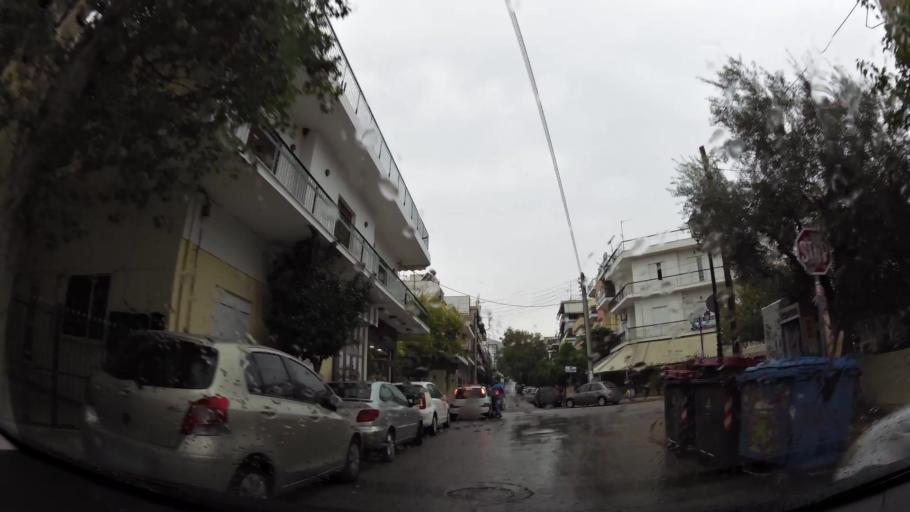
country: GR
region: Attica
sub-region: Nomarchia Athinas
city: Chaidari
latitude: 38.0057
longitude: 23.6603
